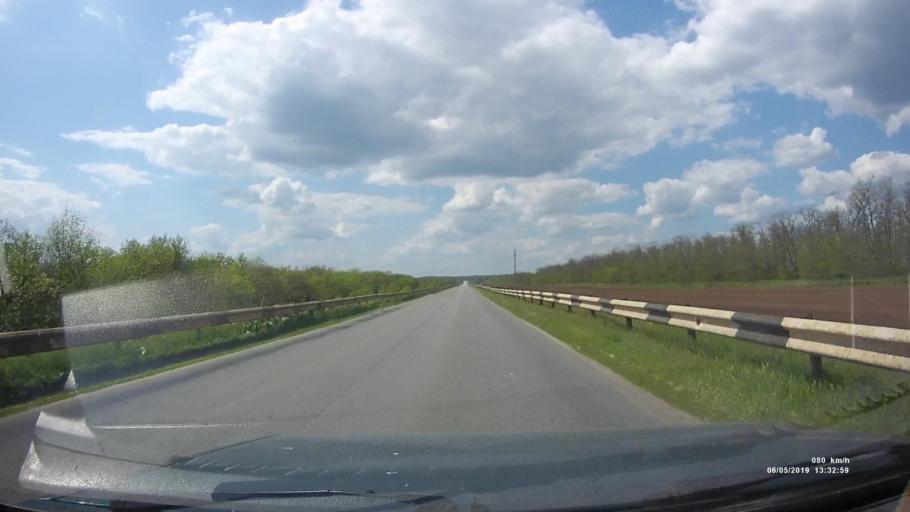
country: RU
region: Rostov
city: Ust'-Donetskiy
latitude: 47.6868
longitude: 40.7867
